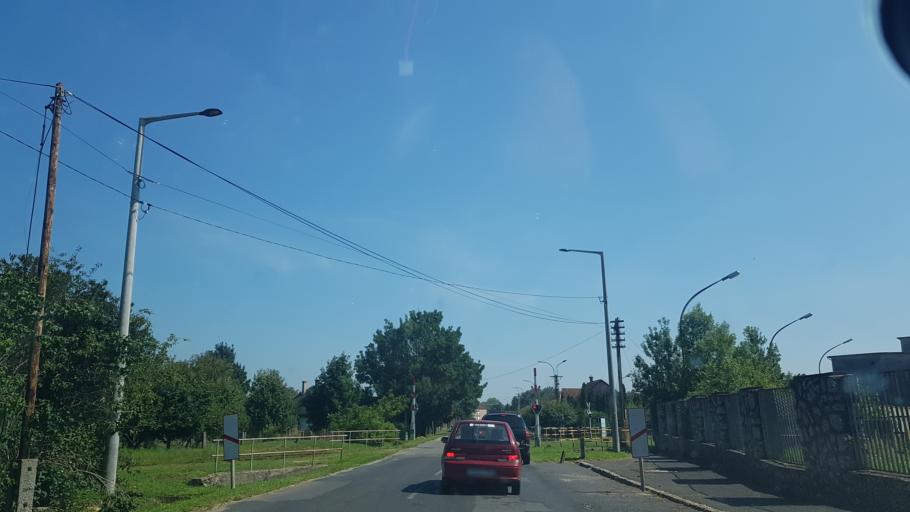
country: HU
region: Somogy
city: Nagyatad
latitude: 46.2335
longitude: 17.3530
